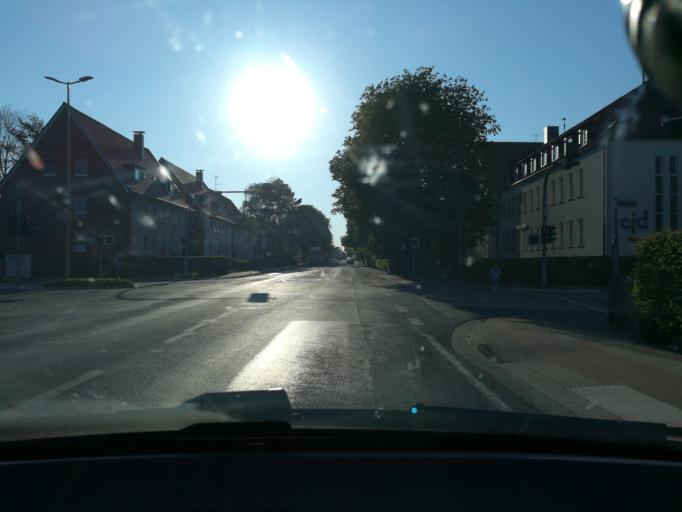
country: DE
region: North Rhine-Westphalia
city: Versmold
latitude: 52.0425
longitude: 8.1610
